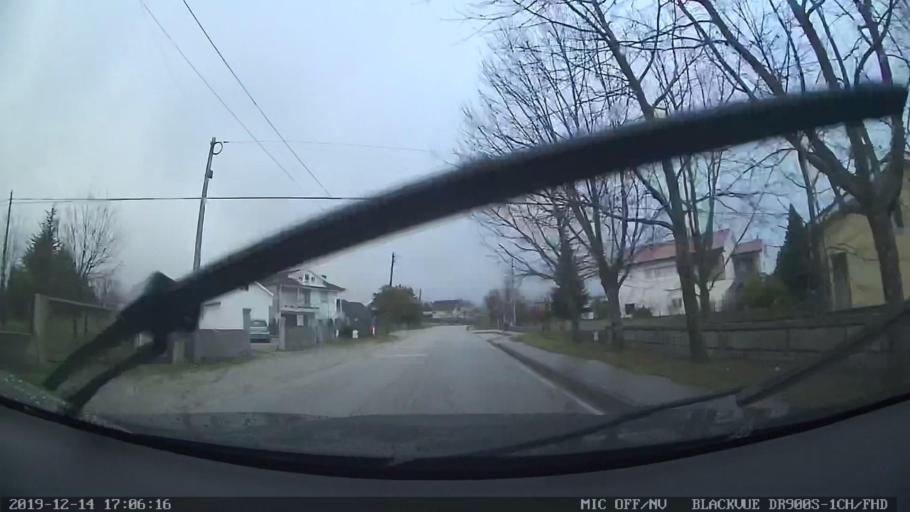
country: PT
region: Vila Real
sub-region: Vila Pouca de Aguiar
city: Vila Pouca de Aguiar
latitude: 41.4549
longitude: -7.5911
